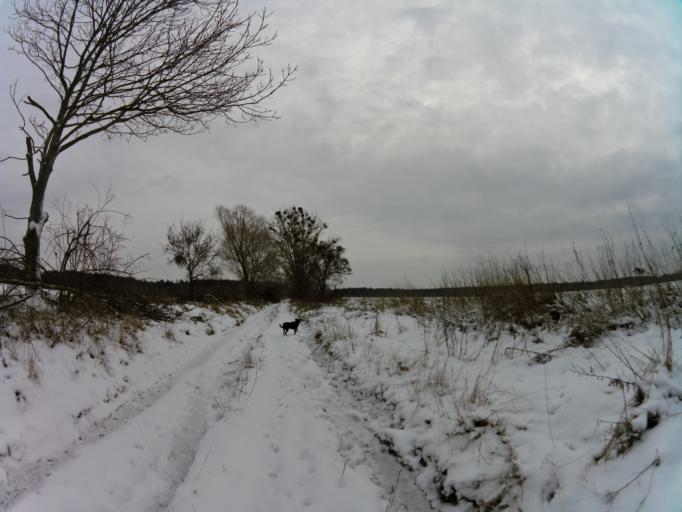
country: PL
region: West Pomeranian Voivodeship
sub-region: Powiat choszczenski
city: Recz
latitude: 53.2703
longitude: 15.5246
